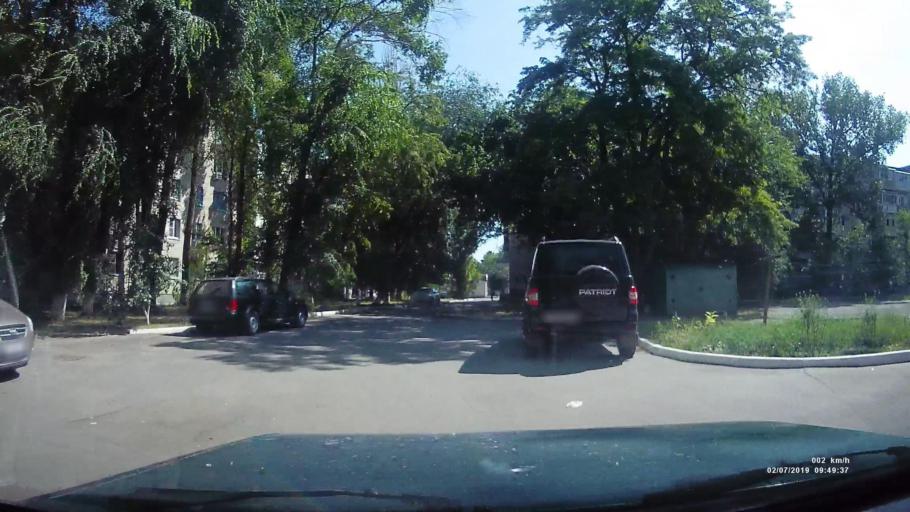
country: RU
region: Rostov
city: Azov
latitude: 47.1032
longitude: 39.4017
